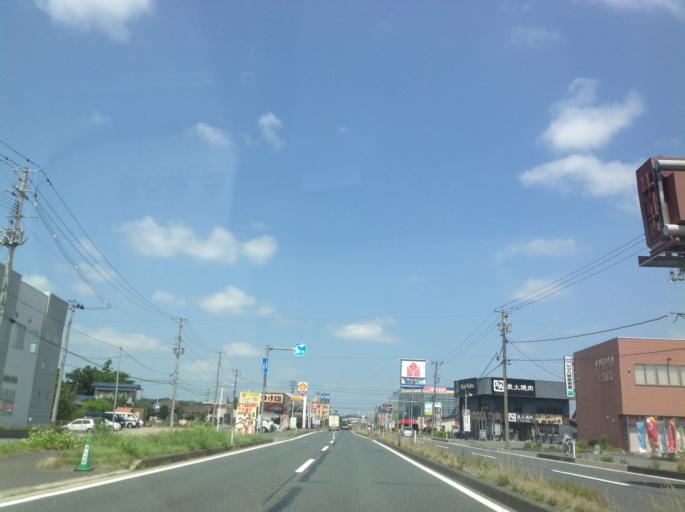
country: JP
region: Iwate
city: Kitakami
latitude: 39.2980
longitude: 141.1068
